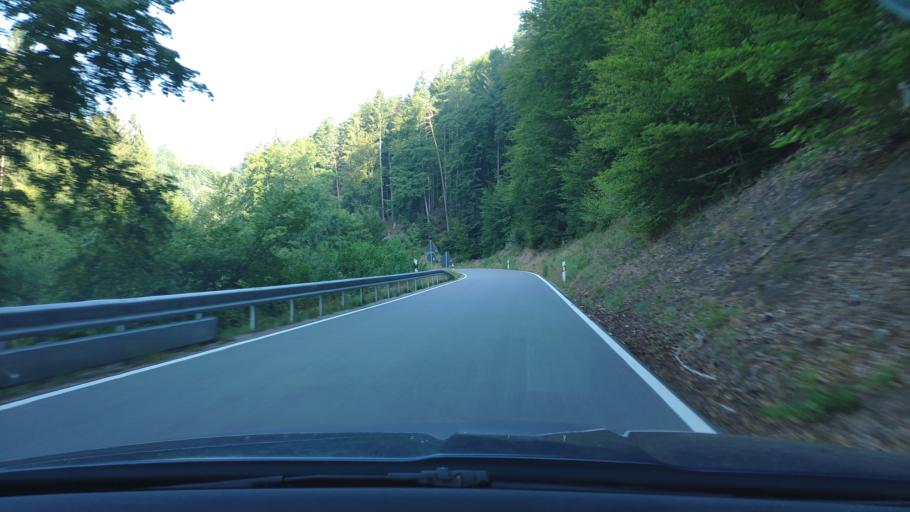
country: DE
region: Rheinland-Pfalz
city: Eppenbrunn
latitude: 49.1045
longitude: 7.6174
